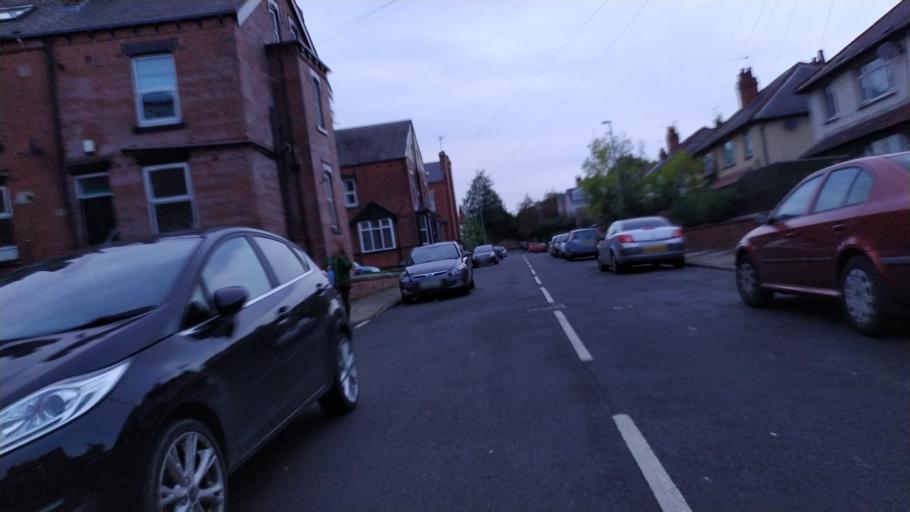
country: GB
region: England
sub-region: City and Borough of Leeds
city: Chapel Allerton
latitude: 53.8175
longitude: -1.5540
